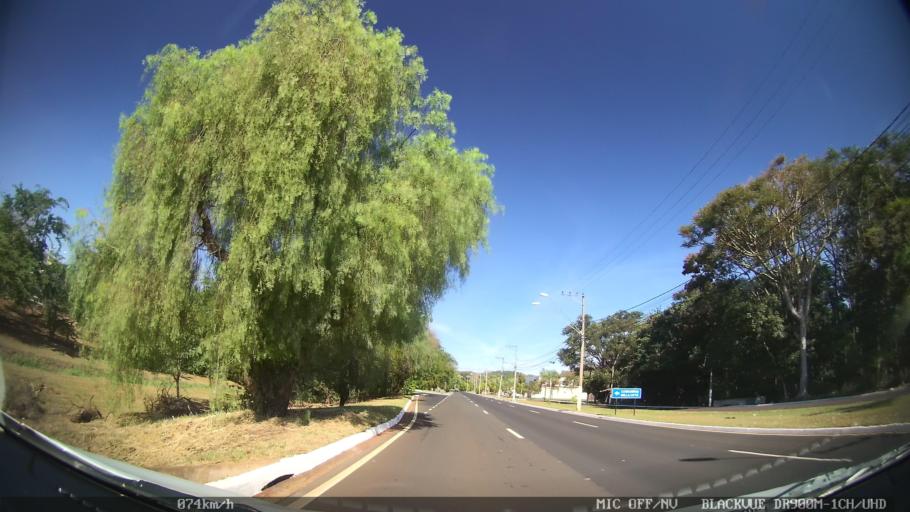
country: BR
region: Sao Paulo
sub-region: Ribeirao Preto
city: Ribeirao Preto
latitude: -21.2348
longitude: -47.7652
